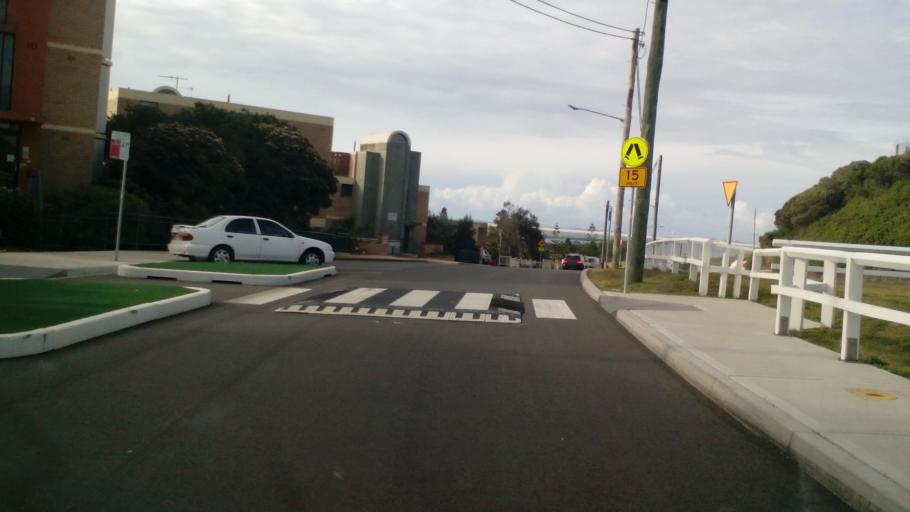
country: AU
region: New South Wales
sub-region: Newcastle
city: Newcastle
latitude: -32.9263
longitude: 151.7901
